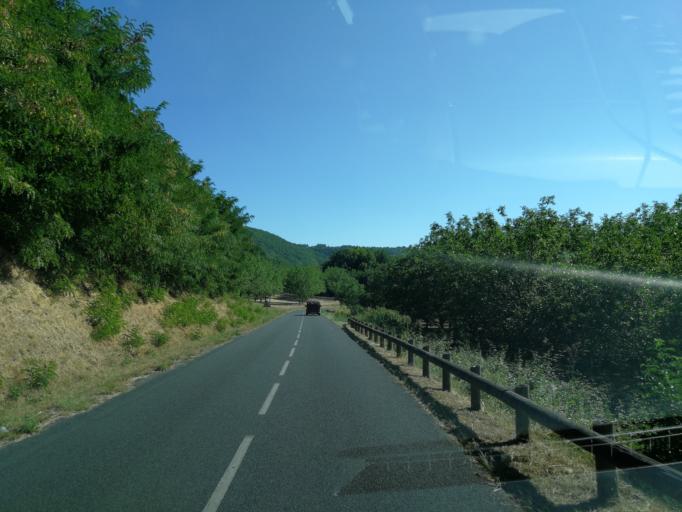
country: FR
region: Midi-Pyrenees
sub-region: Departement du Lot
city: Souillac
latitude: 44.8817
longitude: 1.4479
